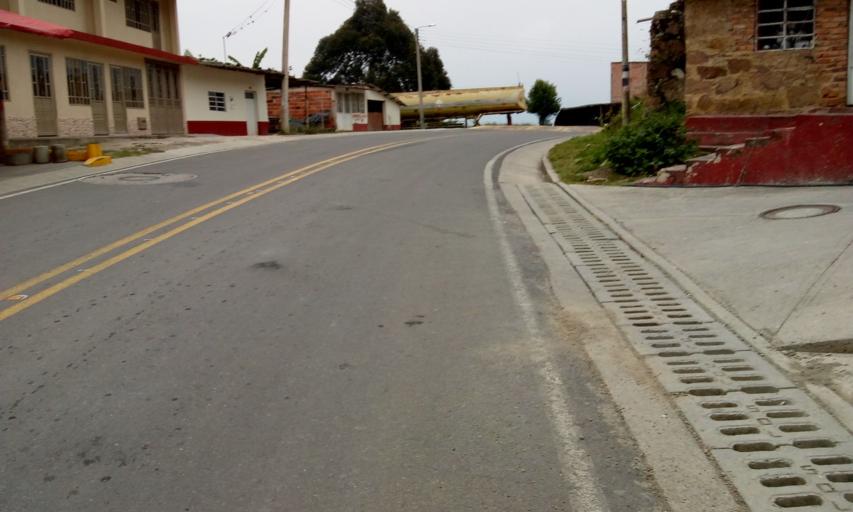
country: CO
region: Boyaca
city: Tipacoque
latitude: 6.4169
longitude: -72.6923
